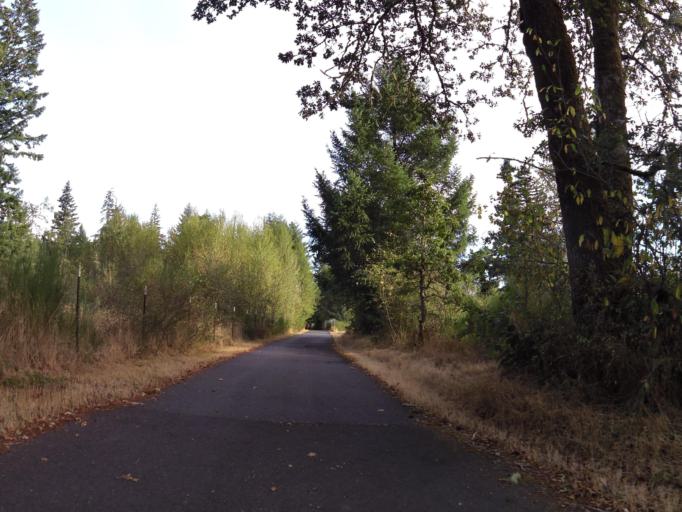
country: US
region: Washington
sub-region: Thurston County
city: Tenino
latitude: 46.9154
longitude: -122.7984
